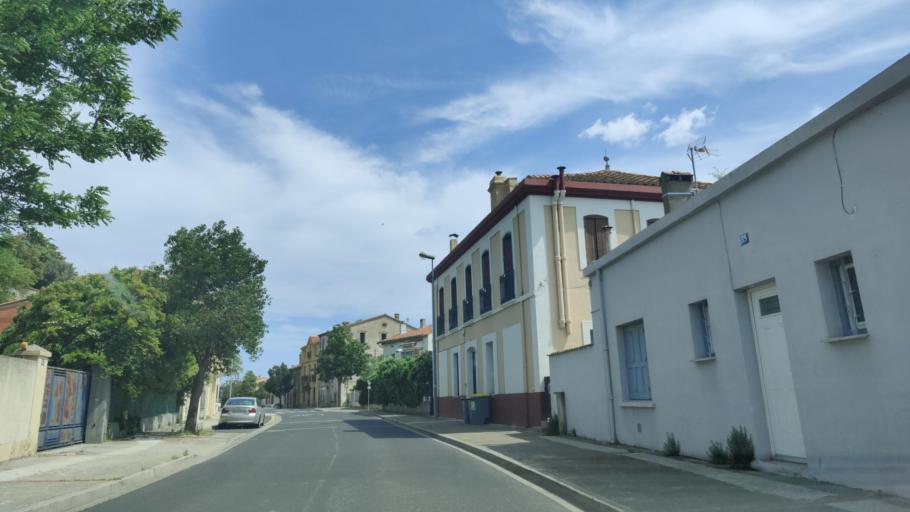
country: FR
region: Languedoc-Roussillon
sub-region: Departement des Pyrenees-Orientales
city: Elne
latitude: 42.5983
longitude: 2.9687
